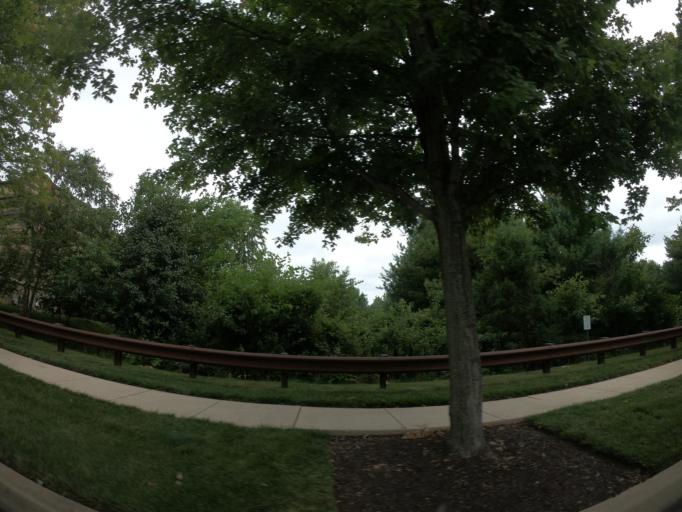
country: US
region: Maryland
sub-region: Howard County
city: Fulton
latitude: 39.1600
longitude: -76.9029
